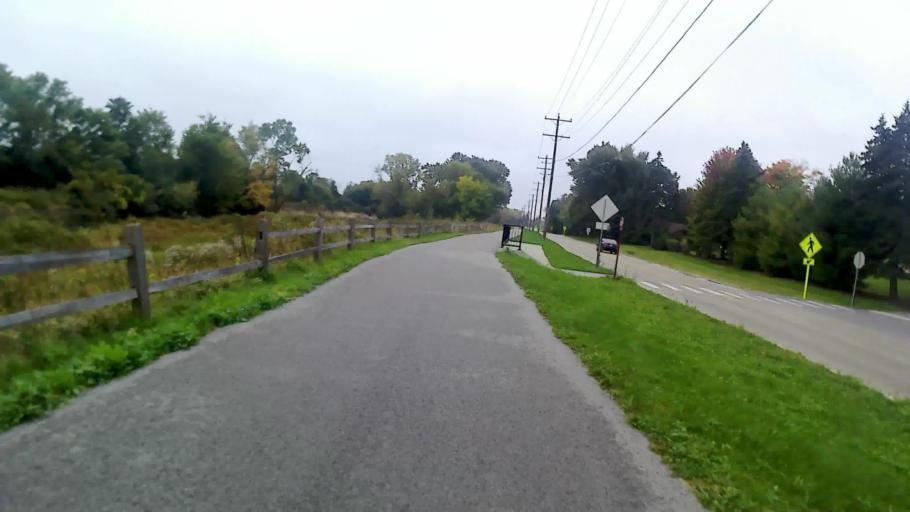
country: US
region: Illinois
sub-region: DuPage County
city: Warrenville
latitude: 41.8143
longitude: -88.1735
